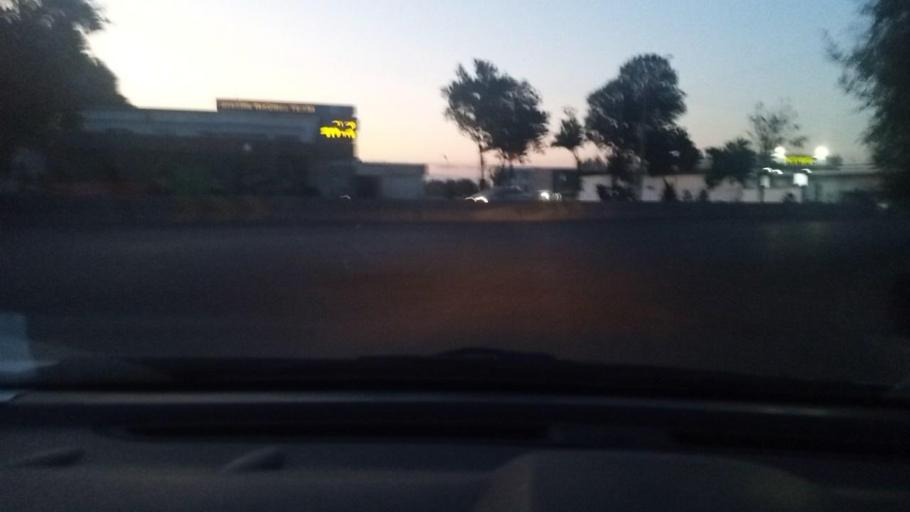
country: UZ
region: Toshkent Shahri
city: Tashkent
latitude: 41.2529
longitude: 69.2167
